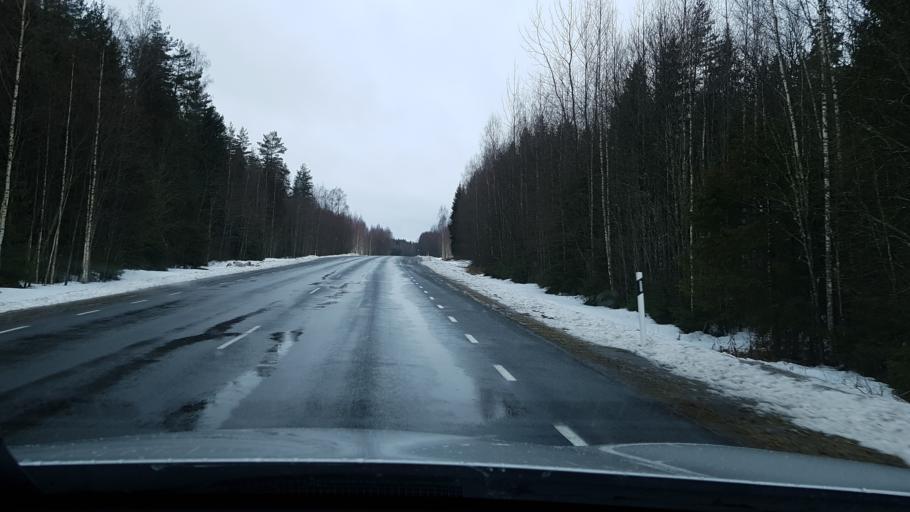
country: LV
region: Apes Novads
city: Ape
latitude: 57.7162
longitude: 26.7651
